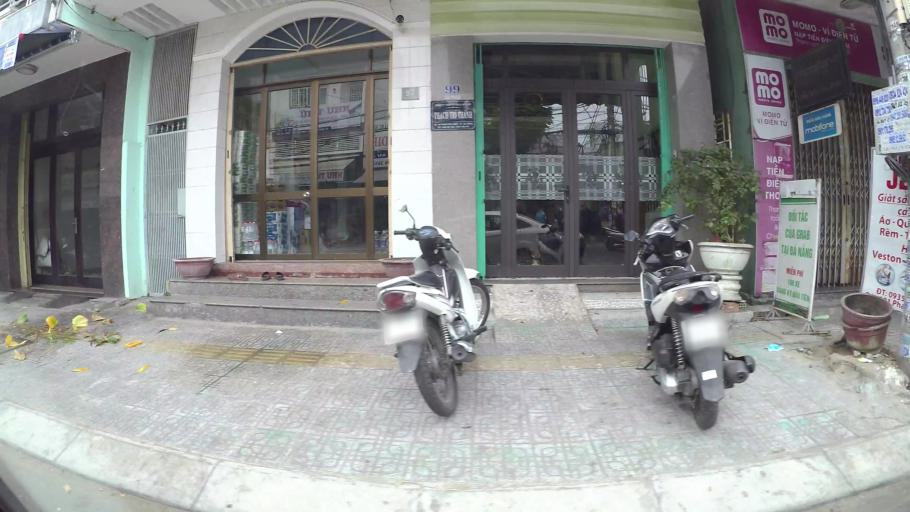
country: VN
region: Da Nang
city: Da Nang
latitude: 16.0564
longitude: 108.2093
